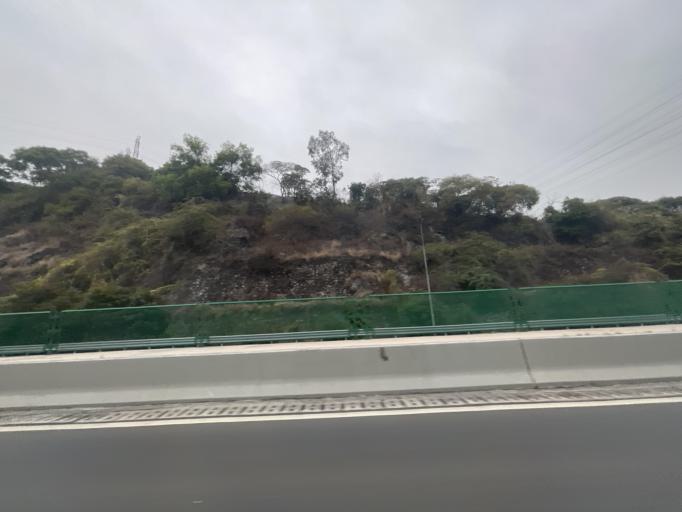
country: CN
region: Guangdong
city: Nansha
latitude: 22.7662
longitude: 113.5607
